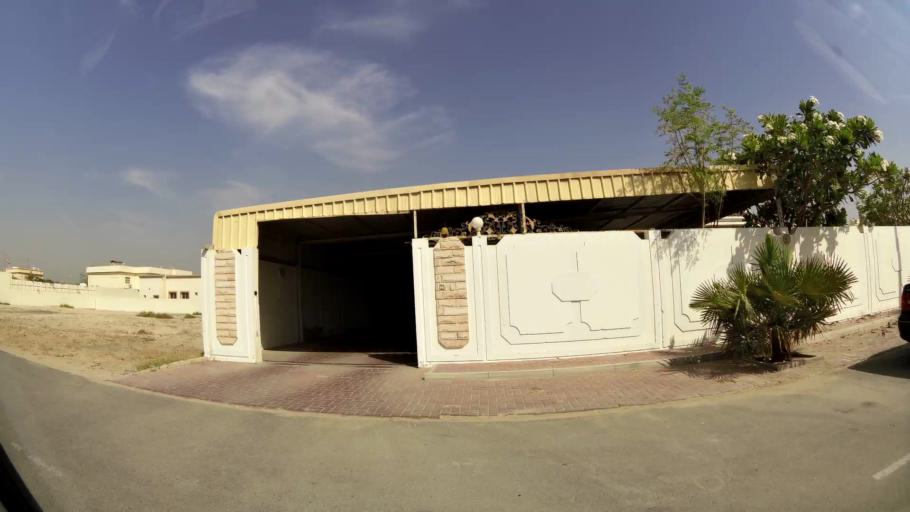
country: AE
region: Ash Shariqah
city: Sharjah
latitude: 25.2674
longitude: 55.4073
